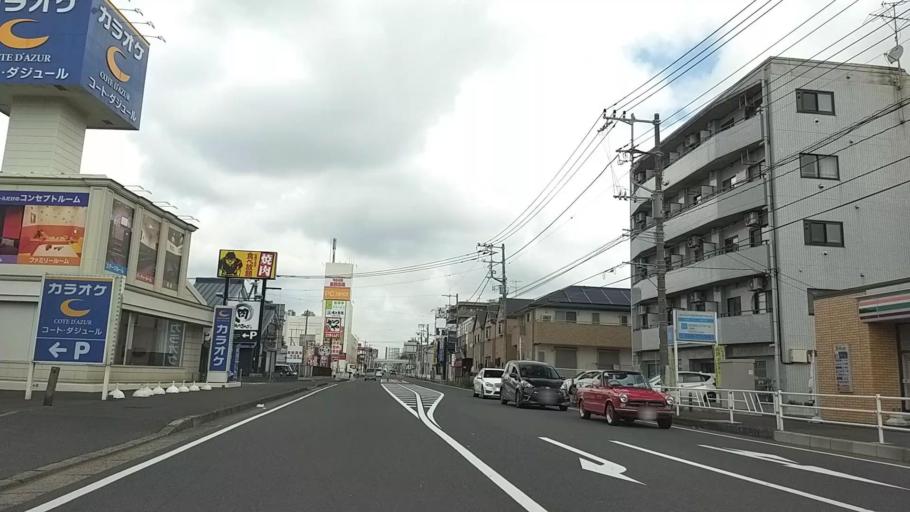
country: JP
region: Kanagawa
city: Minami-rinkan
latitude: 35.5061
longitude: 139.4632
